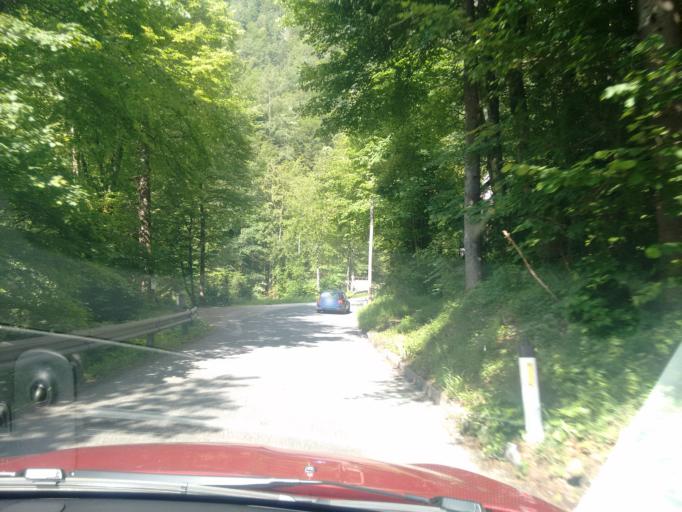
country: AT
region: Upper Austria
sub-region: Politischer Bezirk Gmunden
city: Ebensee
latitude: 47.8137
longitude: 13.7511
